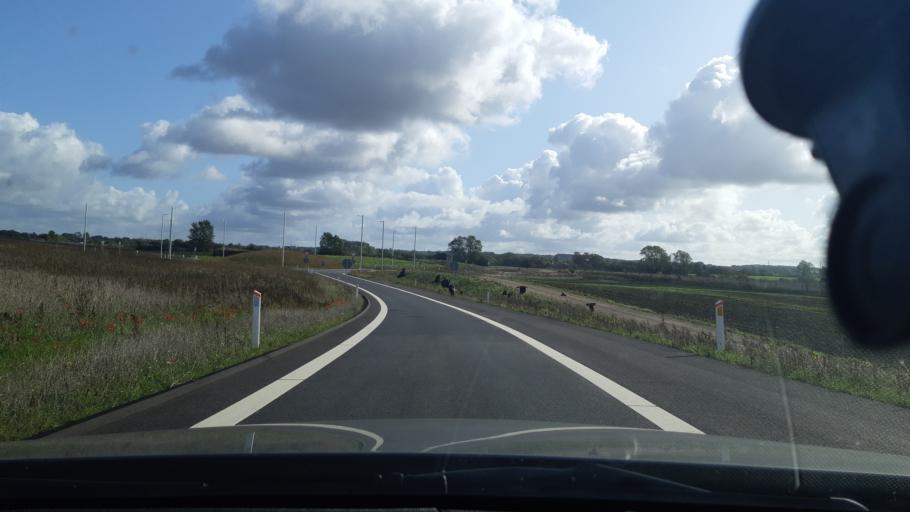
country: DK
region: Zealand
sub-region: Holbaek Kommune
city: Holbaek
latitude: 55.6577
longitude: 11.6289
